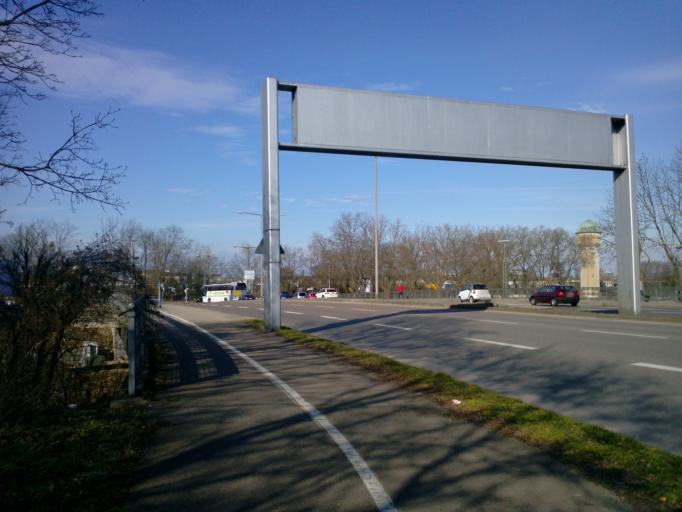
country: DE
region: Baden-Wuerttemberg
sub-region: Karlsruhe Region
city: Karlsruhe
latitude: 48.9910
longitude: 8.4036
